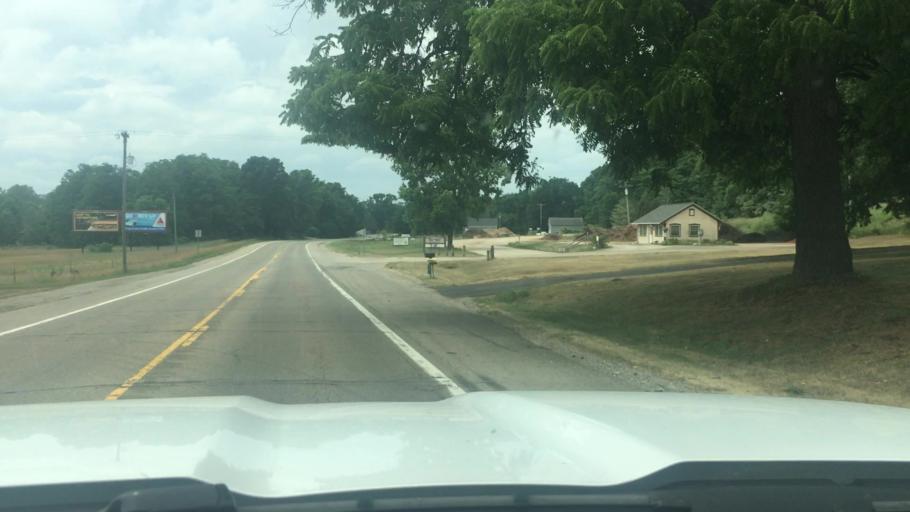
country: US
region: Michigan
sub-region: Kent County
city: Forest Hills
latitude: 42.9282
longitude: -85.4281
